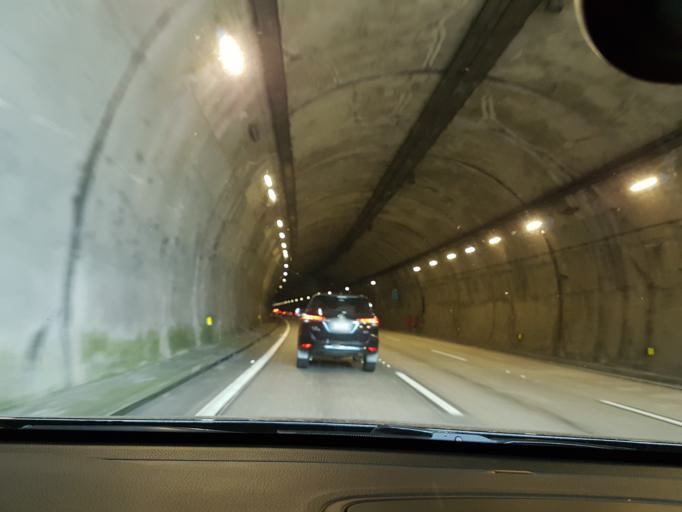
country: BR
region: Sao Paulo
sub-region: Cubatao
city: Cubatao
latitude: -23.8956
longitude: -46.5074
